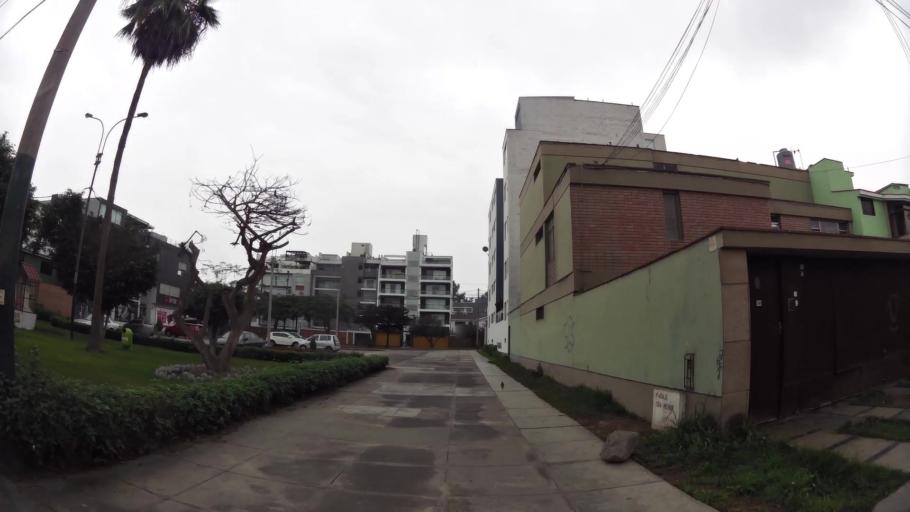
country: PE
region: Lima
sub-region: Lima
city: Surco
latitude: -12.1257
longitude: -76.9905
